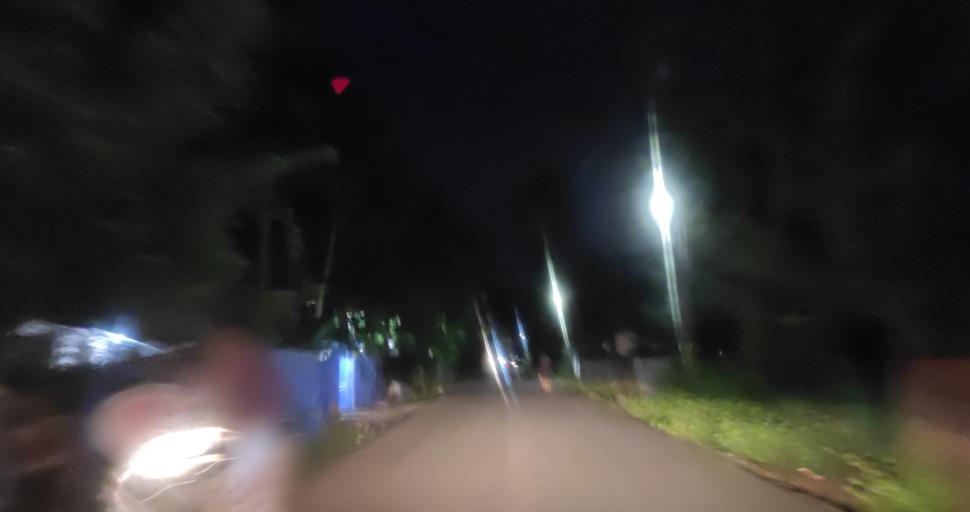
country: IN
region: Kerala
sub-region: Alappuzha
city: Vayalar
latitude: 9.6793
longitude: 76.3034
